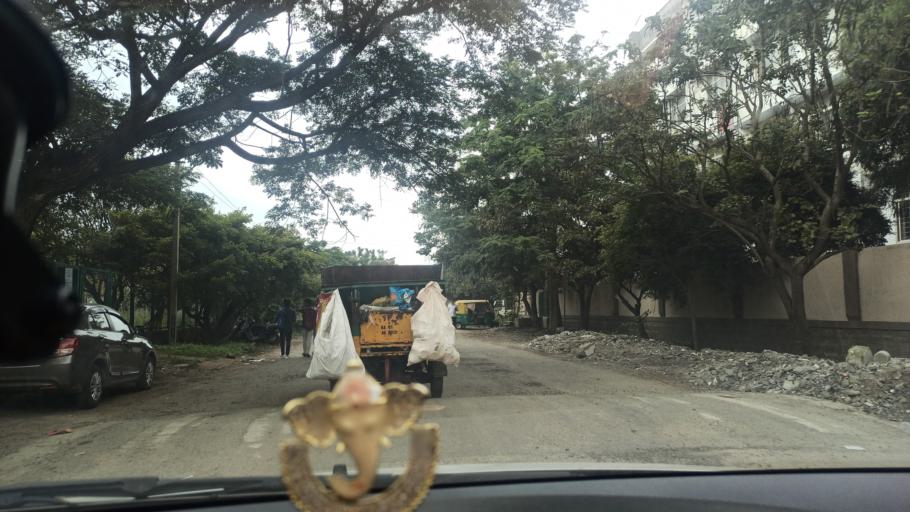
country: IN
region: Karnataka
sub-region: Bangalore Urban
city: Bangalore
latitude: 12.9167
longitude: 77.6418
